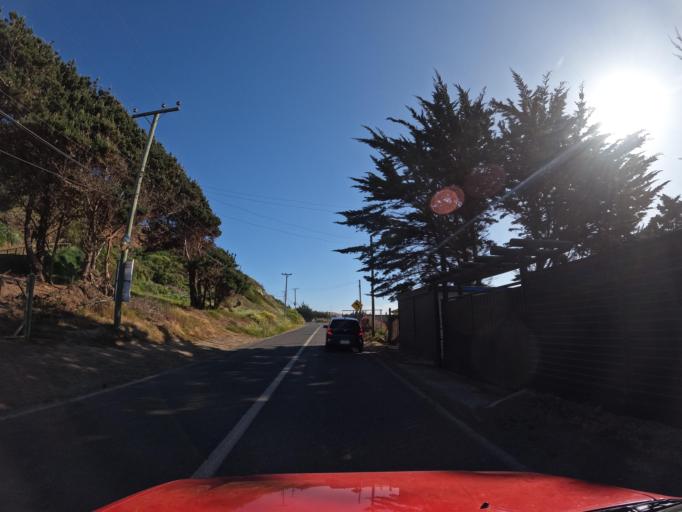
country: CL
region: Maule
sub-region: Provincia de Talca
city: Constitucion
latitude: -34.8697
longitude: -72.1503
